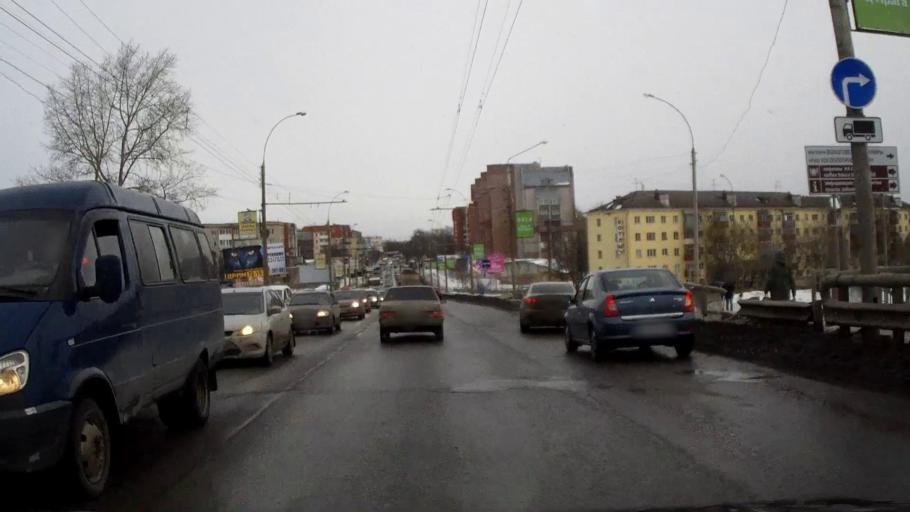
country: RU
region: Vologda
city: Vologda
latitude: 59.2173
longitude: 39.8634
